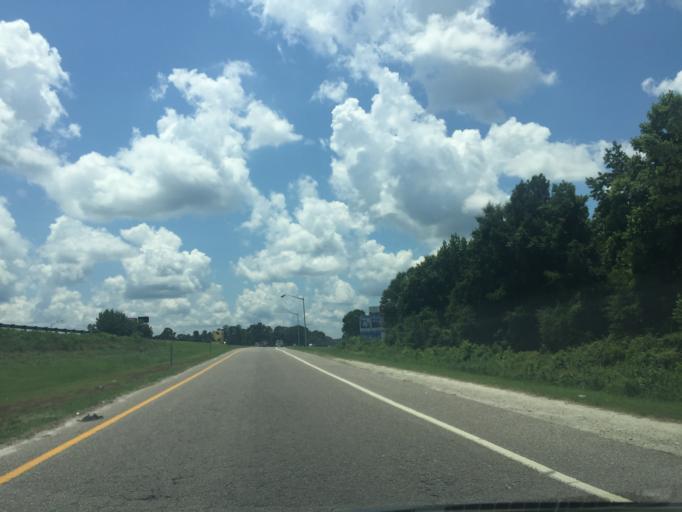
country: US
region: South Carolina
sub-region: Jasper County
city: Ridgeland
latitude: 32.4769
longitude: -80.9723
